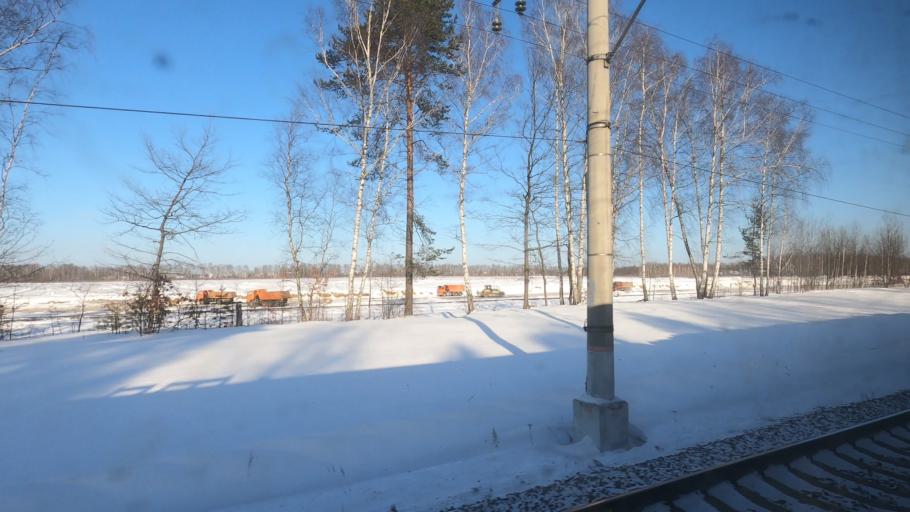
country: RU
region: Moskovskaya
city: Imeni Vorovskogo
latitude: 55.7226
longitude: 38.2726
